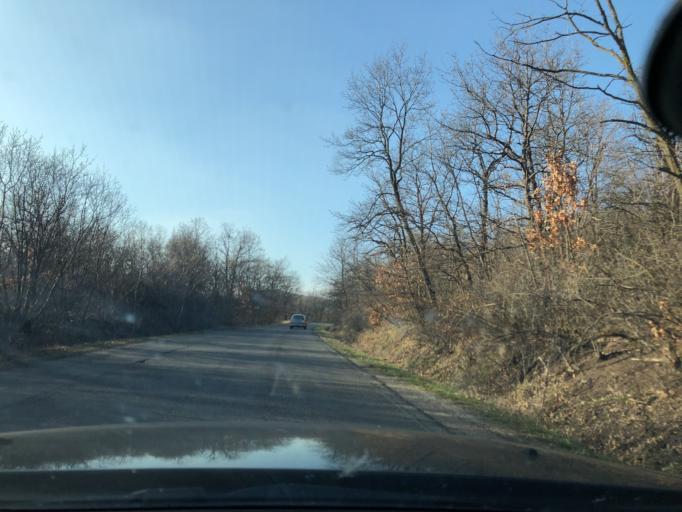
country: HU
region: Nograd
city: Paszto
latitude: 47.9235
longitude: 19.6312
